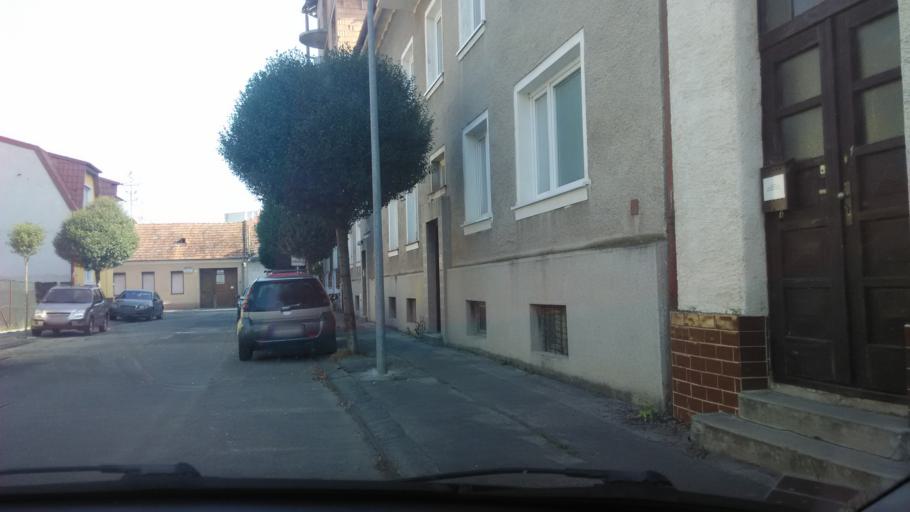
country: SK
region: Trnavsky
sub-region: Okres Trnava
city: Piestany
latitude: 48.5937
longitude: 17.8316
